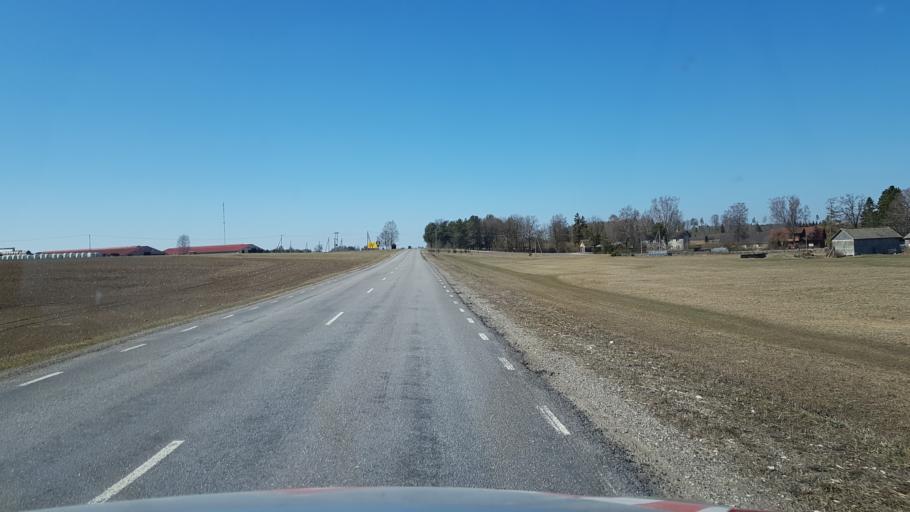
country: EE
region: Laeaene-Virumaa
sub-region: Tamsalu vald
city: Tamsalu
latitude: 59.1629
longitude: 26.1852
